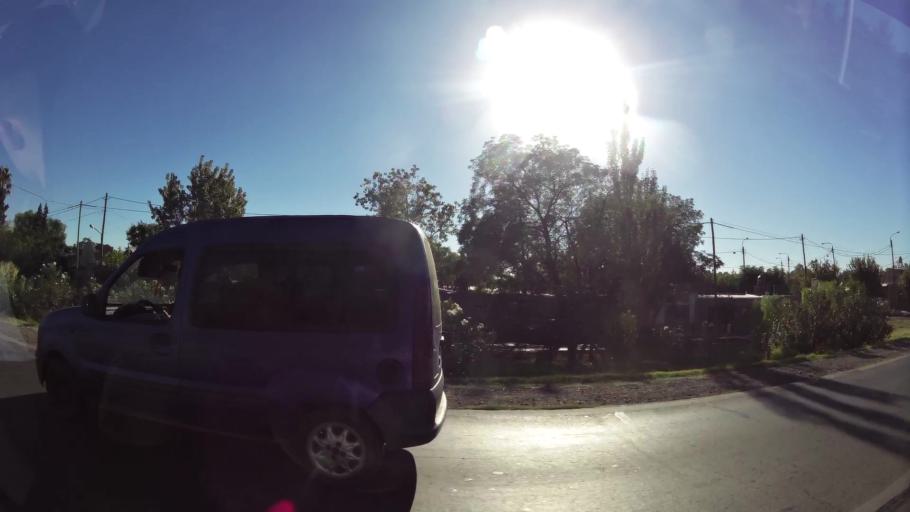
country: AR
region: Mendoza
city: Las Heras
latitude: -32.8361
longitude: -68.8058
